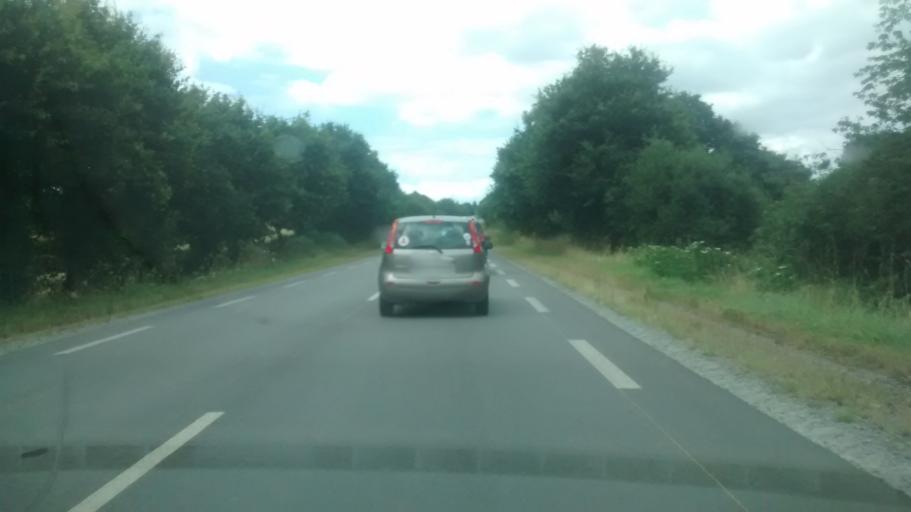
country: FR
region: Brittany
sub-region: Departement du Morbihan
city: Mauron
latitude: 48.0889
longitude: -2.2691
